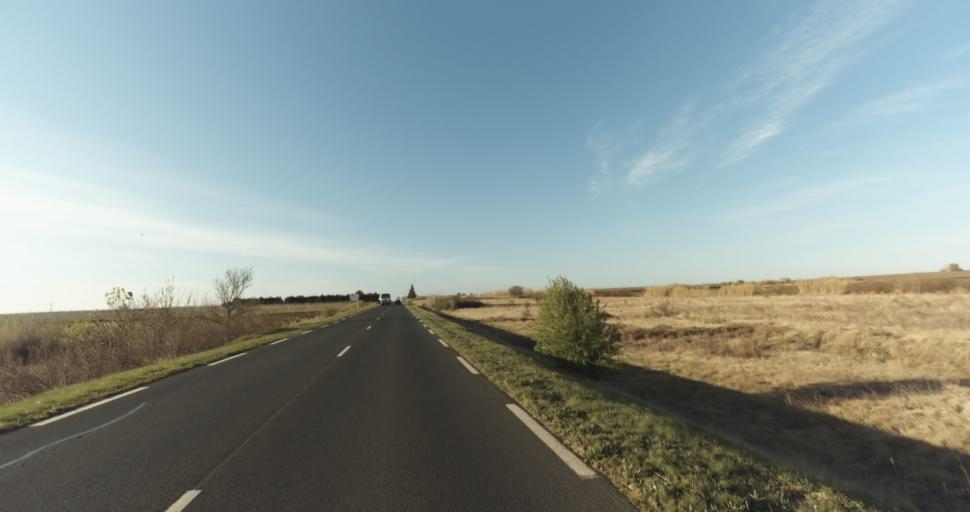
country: FR
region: Languedoc-Roussillon
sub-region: Departement de l'Herault
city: Marseillan
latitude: 43.3799
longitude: 3.5350
